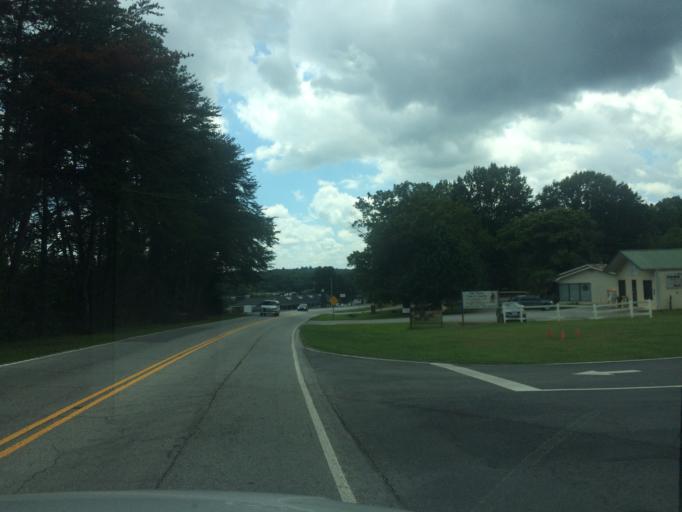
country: US
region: South Carolina
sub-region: Spartanburg County
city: Inman
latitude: 35.1174
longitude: -82.0414
